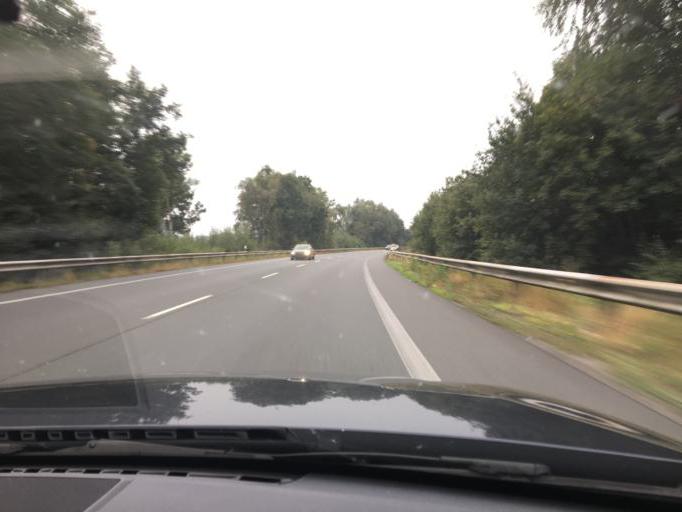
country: DE
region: North Rhine-Westphalia
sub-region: Regierungsbezirk Munster
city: Muenster
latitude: 52.0421
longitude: 7.6857
